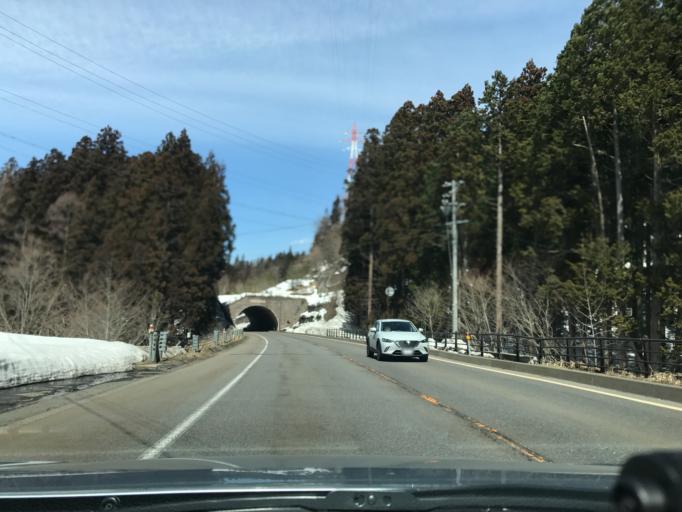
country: JP
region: Nagano
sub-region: Kitaazumi Gun
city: Hakuba
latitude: 36.6148
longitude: 137.8617
